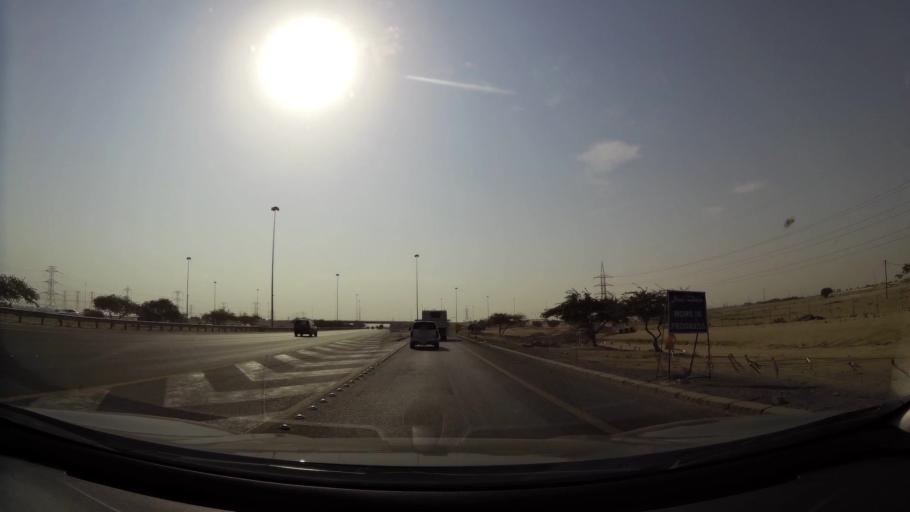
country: KW
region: Al Ahmadi
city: Al Ahmadi
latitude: 28.9629
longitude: 48.1190
